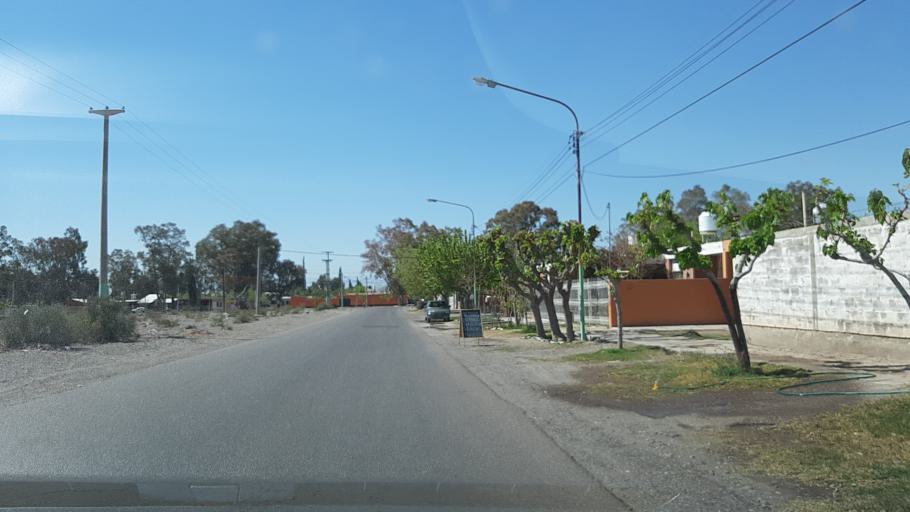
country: AR
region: San Juan
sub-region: Departamento de Rivadavia
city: Rivadavia
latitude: -31.5225
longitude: -68.6269
